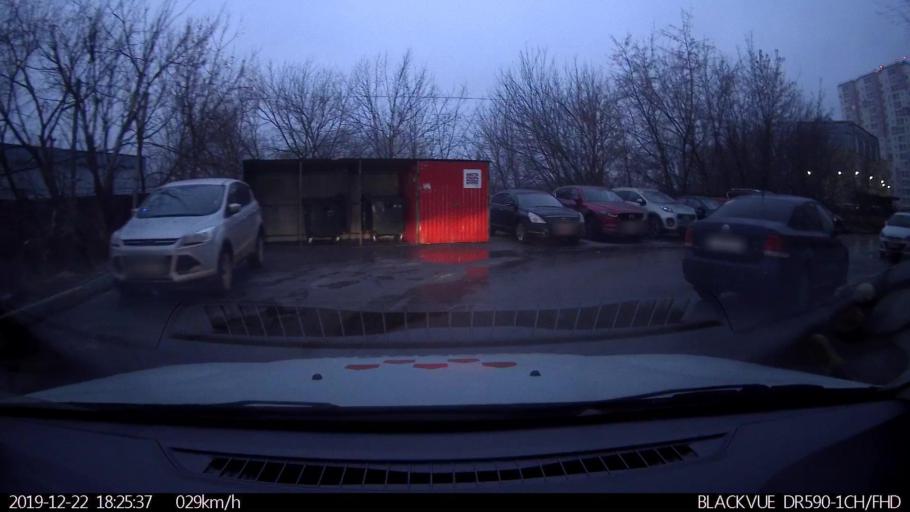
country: RU
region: Nizjnij Novgorod
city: Bor
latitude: 56.3154
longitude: 44.0640
